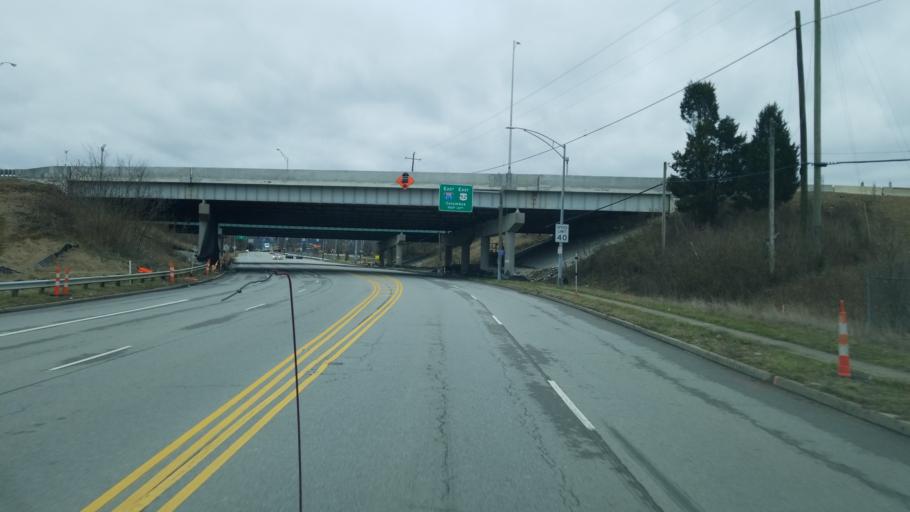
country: US
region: Kentucky
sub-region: Campbell County
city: Fort Thomas
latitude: 39.0615
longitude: -84.4221
